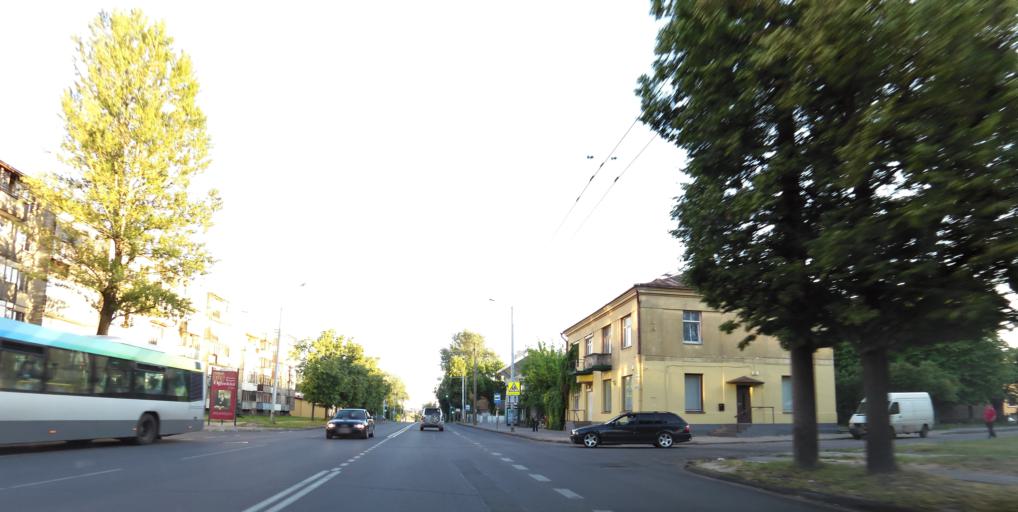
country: LT
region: Vilnius County
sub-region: Vilnius
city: Vilnius
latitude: 54.7081
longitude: 25.2853
